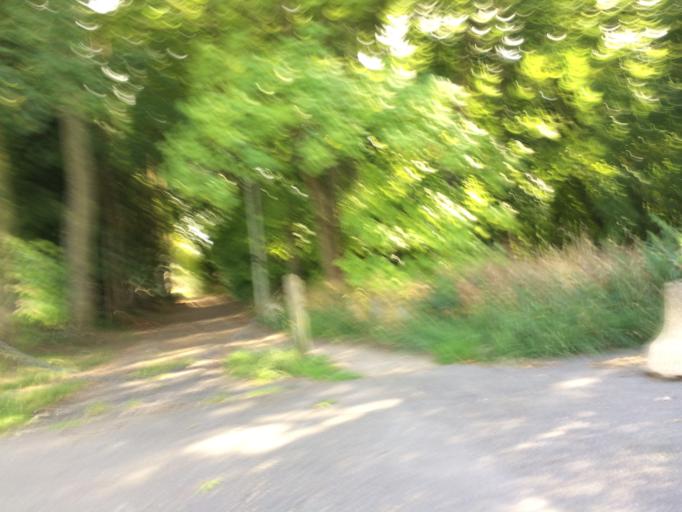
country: FR
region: Ile-de-France
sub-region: Departement de l'Essonne
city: Saulx-les-Chartreux
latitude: 48.6913
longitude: 2.2754
